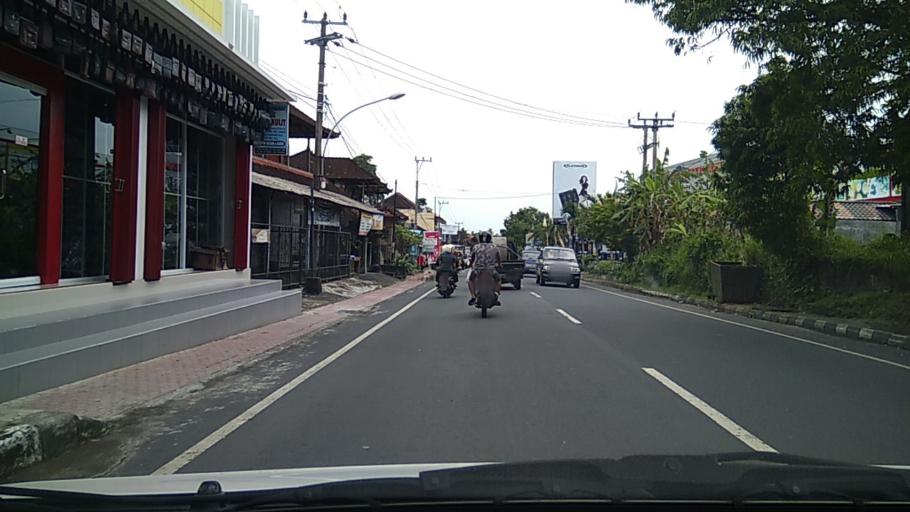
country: ID
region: Bali
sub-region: Kabupaten Gianyar
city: Ubud
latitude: -8.5349
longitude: 115.3076
